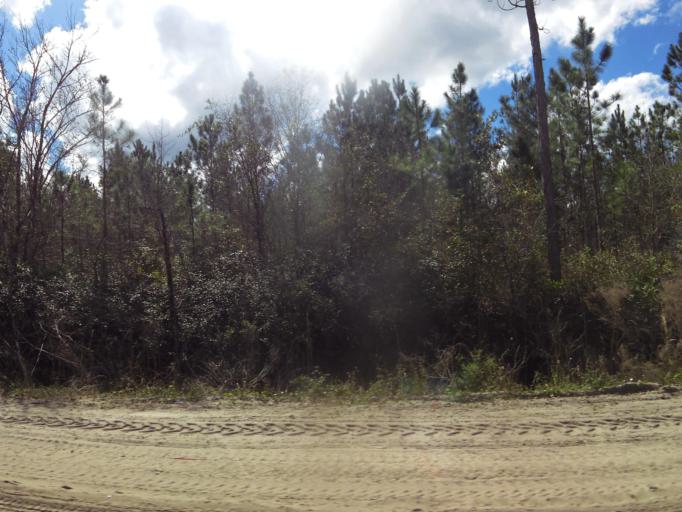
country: US
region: Florida
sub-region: Clay County
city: Green Cove Springs
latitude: 29.8368
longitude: -81.7753
